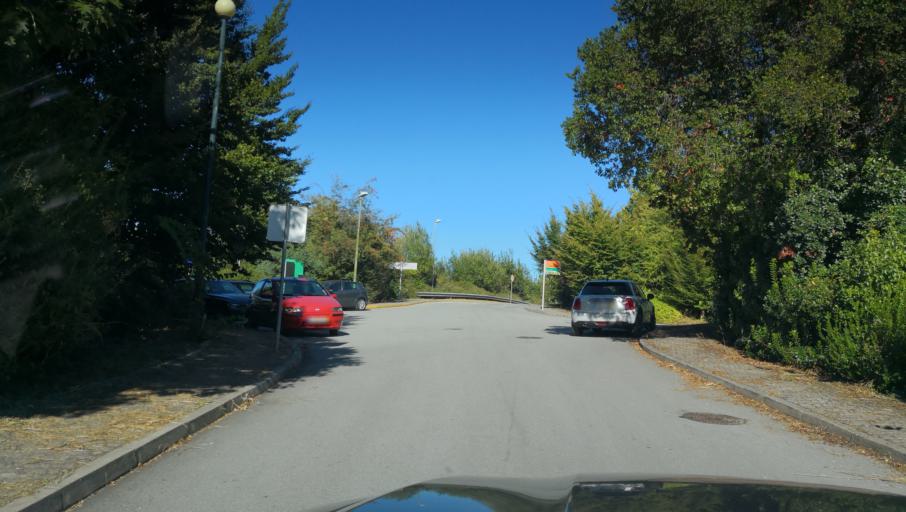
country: PT
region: Vila Real
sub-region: Vila Real
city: Vila Real
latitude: 41.2889
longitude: -7.7407
